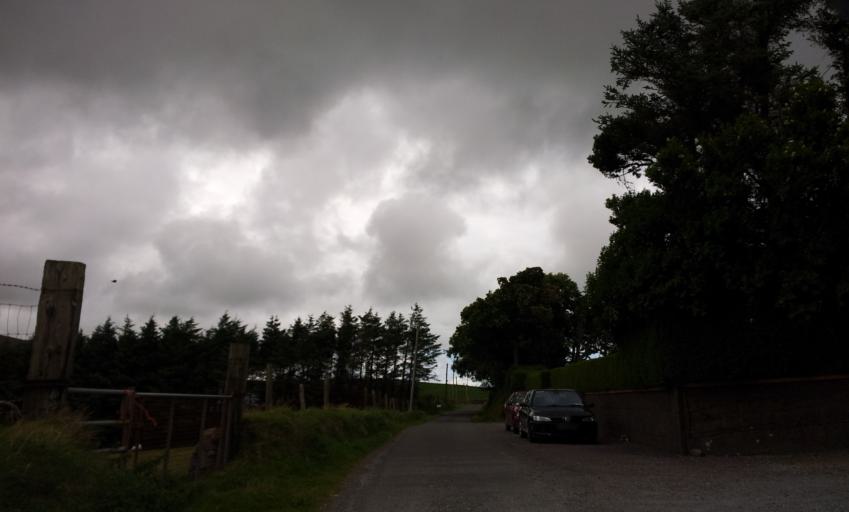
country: IE
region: Munster
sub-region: Ciarrai
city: Killorglin
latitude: 52.1951
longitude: -9.9288
